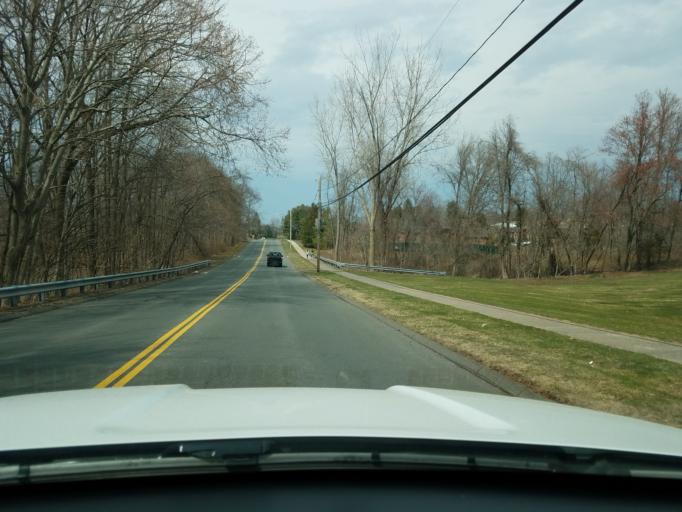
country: US
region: Connecticut
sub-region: Hartford County
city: Newington
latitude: 41.6590
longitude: -72.7165
